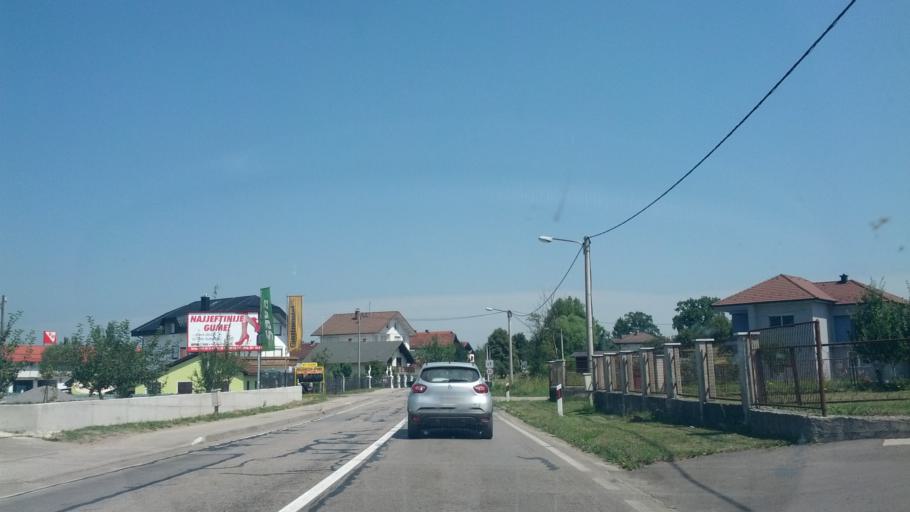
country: BA
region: Federation of Bosnia and Herzegovina
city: Bihac
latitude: 44.8419
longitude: 15.8280
